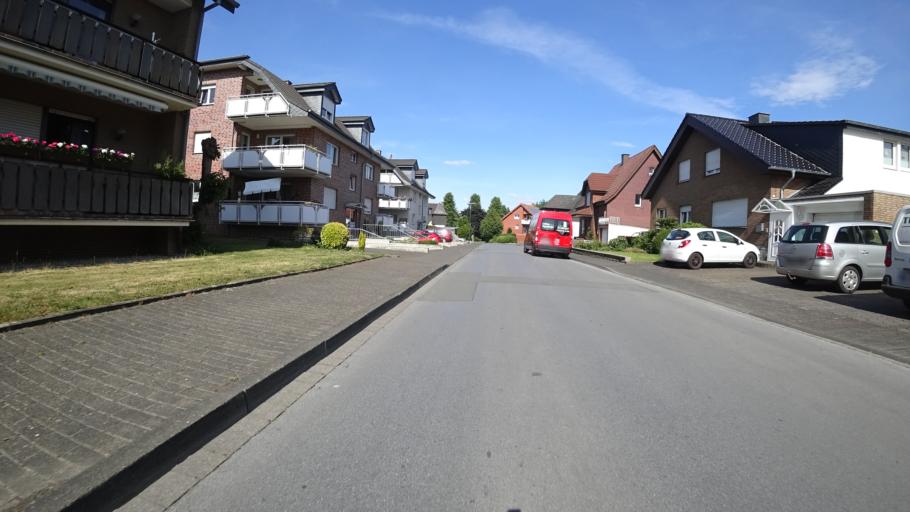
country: DE
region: North Rhine-Westphalia
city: Erwitte
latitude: 51.6267
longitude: 8.3630
